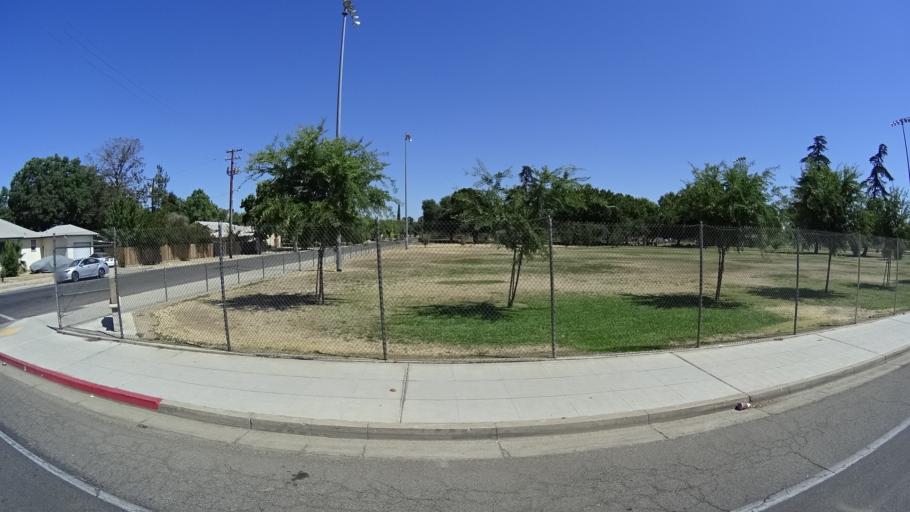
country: US
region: California
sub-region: Fresno County
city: Fresno
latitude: 36.7866
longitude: -119.8219
